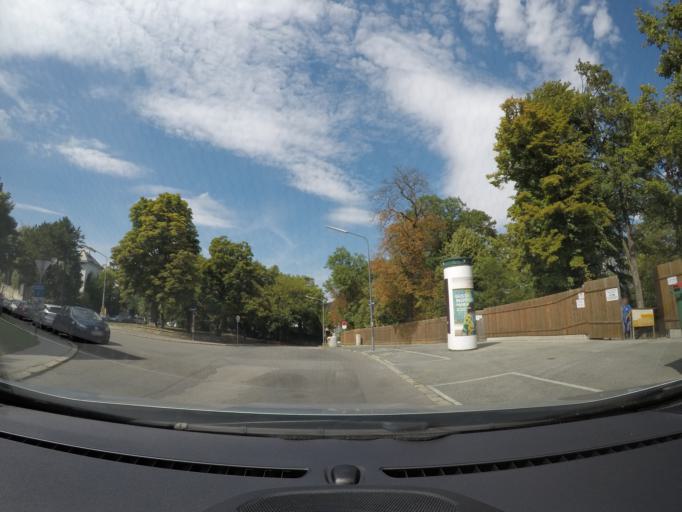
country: AT
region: Lower Austria
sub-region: Politischer Bezirk Modling
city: Perchtoldsdorf
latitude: 48.1908
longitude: 16.2624
